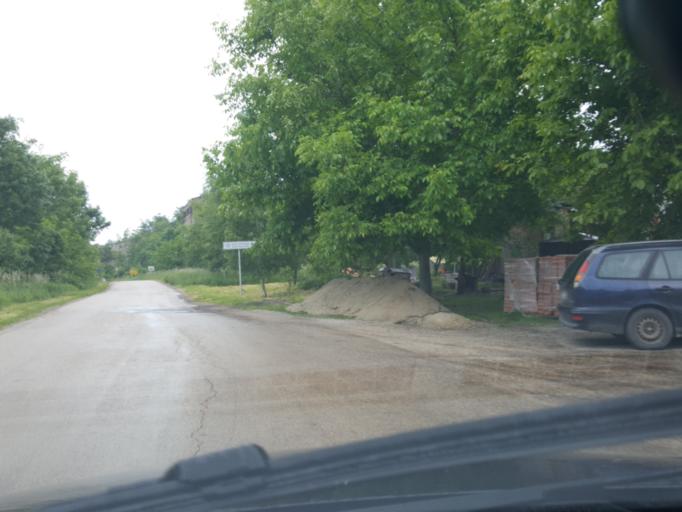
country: RS
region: Central Serbia
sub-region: Zajecarski Okrug
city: Boljevac
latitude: 43.7721
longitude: 21.9341
